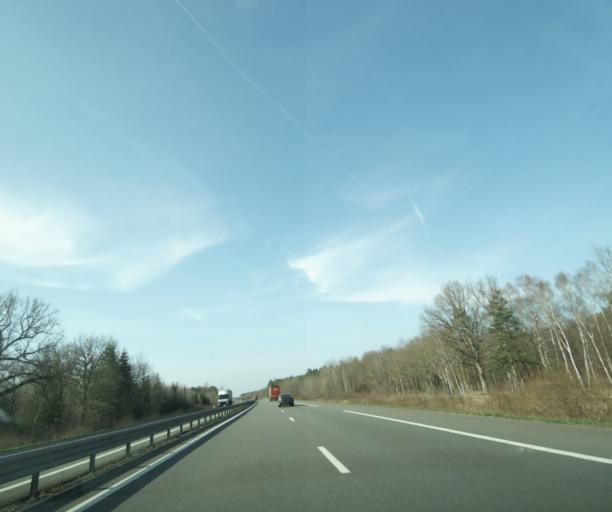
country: FR
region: Centre
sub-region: Departement du Loir-et-Cher
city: Salbris
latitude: 47.3926
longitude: 2.0439
